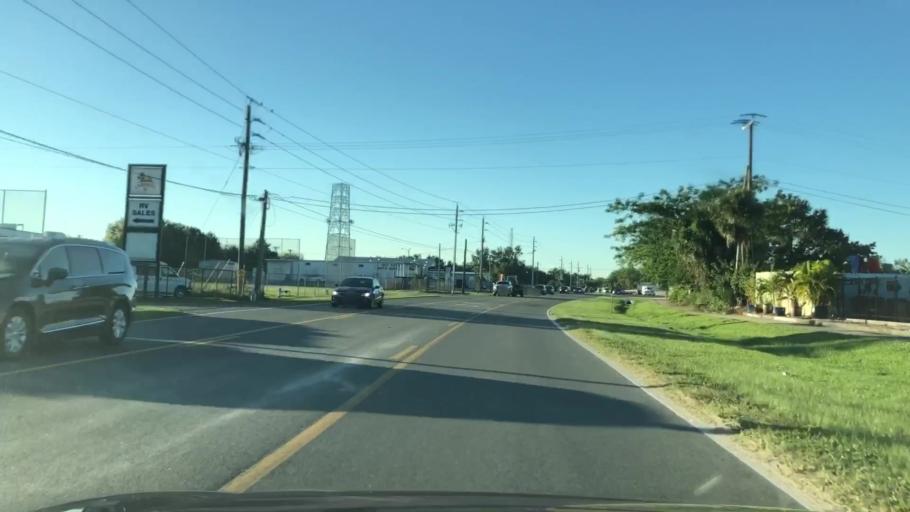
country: US
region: Florida
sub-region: Sarasota County
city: Fruitville
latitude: 27.3309
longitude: -82.4494
